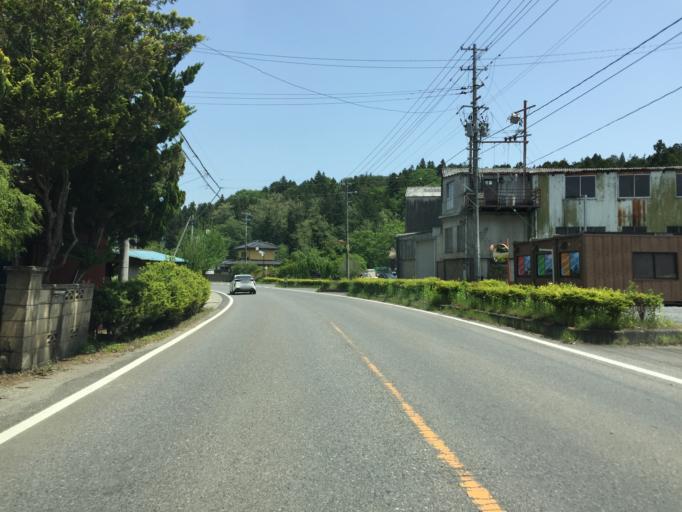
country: JP
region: Fukushima
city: Ishikawa
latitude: 37.1137
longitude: 140.3366
